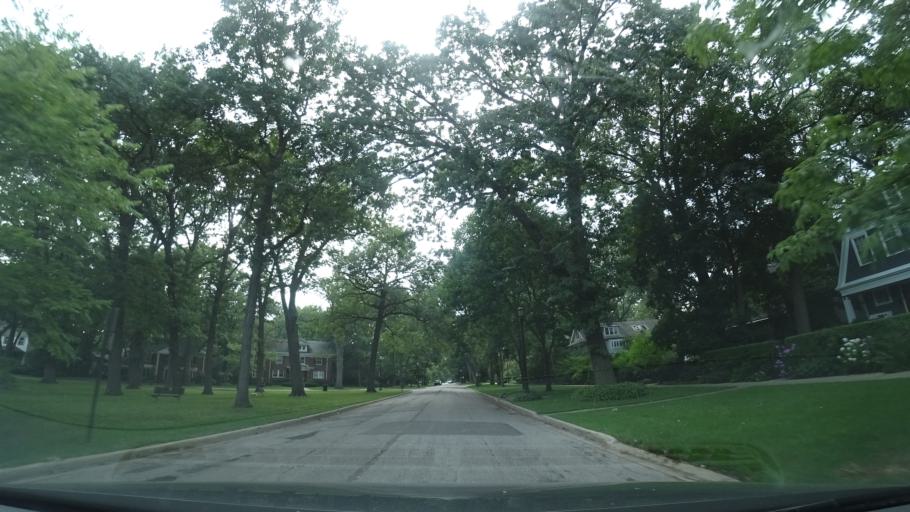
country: US
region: Illinois
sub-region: Cook County
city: Wilmette
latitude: 42.0621
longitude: -87.7054
